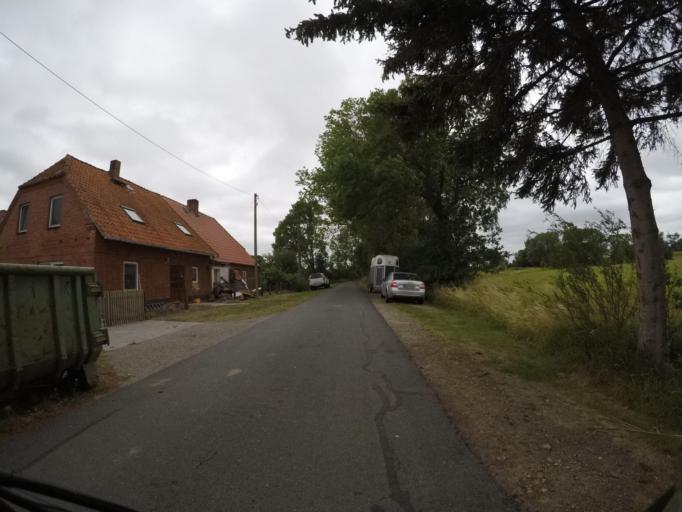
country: DE
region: Lower Saxony
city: Hitzacker
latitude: 53.1516
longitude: 11.0832
